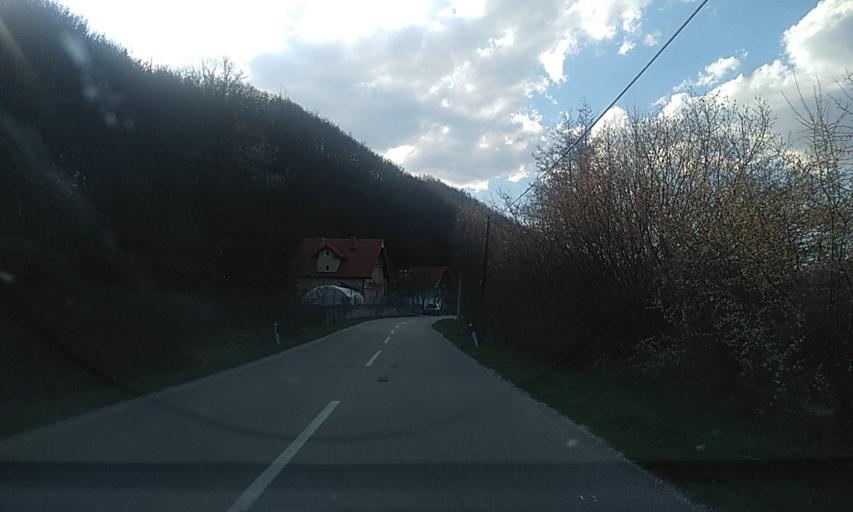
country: RS
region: Central Serbia
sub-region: Pcinjski Okrug
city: Bosilegrad
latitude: 42.4524
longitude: 22.4989
